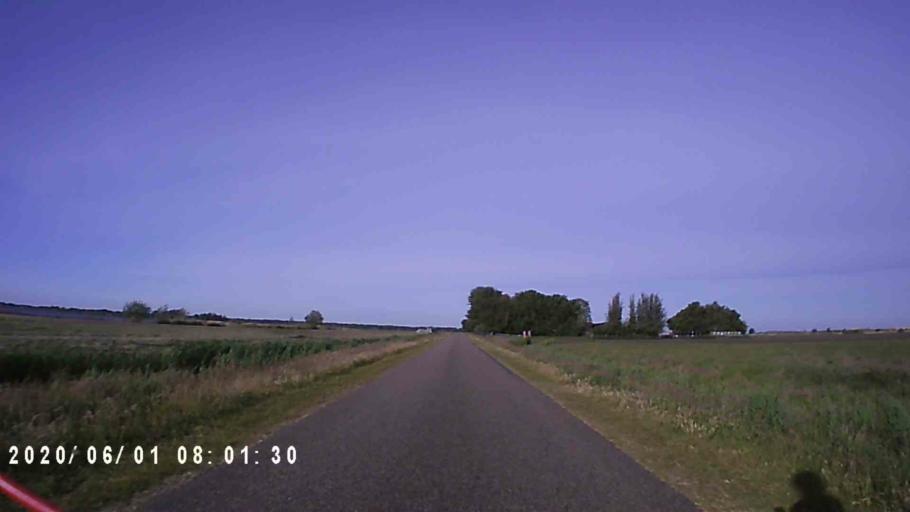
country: NL
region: Friesland
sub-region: Gemeente Dantumadiel
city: Rinsumageast
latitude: 53.2808
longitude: 5.9299
